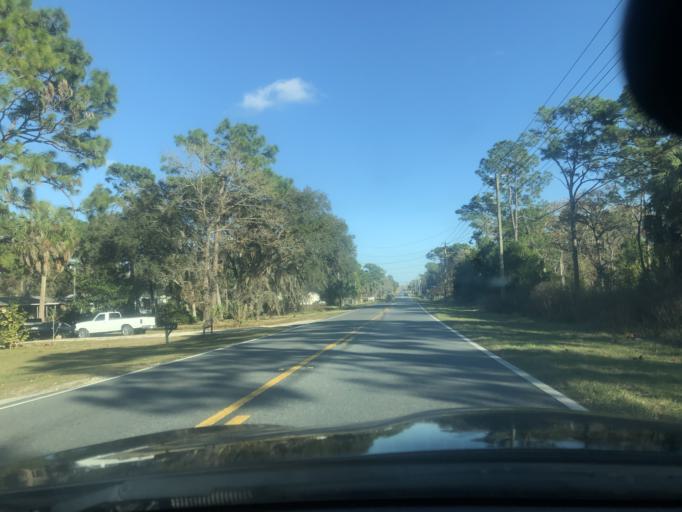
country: US
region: Florida
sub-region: Citrus County
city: Sugarmill Woods
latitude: 28.7640
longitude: -82.5357
